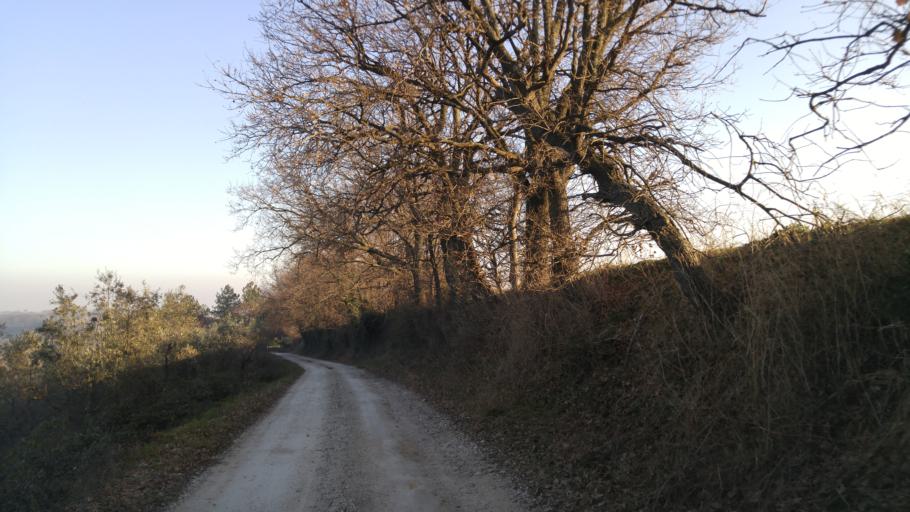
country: IT
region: The Marches
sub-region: Provincia di Pesaro e Urbino
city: Fenile
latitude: 43.8537
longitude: 12.9618
